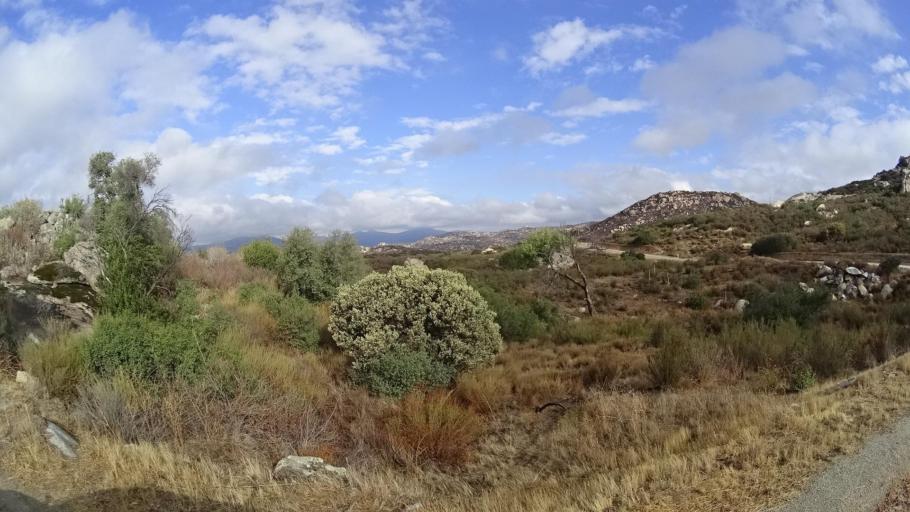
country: MX
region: Baja California
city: Tecate
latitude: 32.6421
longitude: -116.6353
